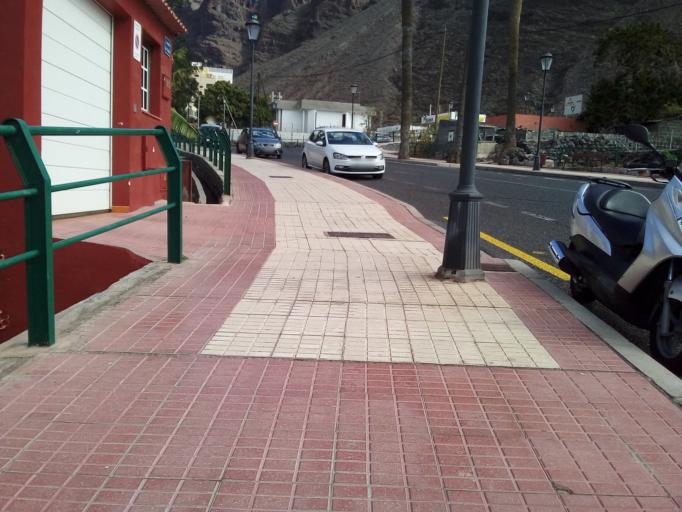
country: ES
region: Canary Islands
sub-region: Provincia de Santa Cruz de Tenerife
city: Alajero
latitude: 28.0945
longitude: -17.3368
